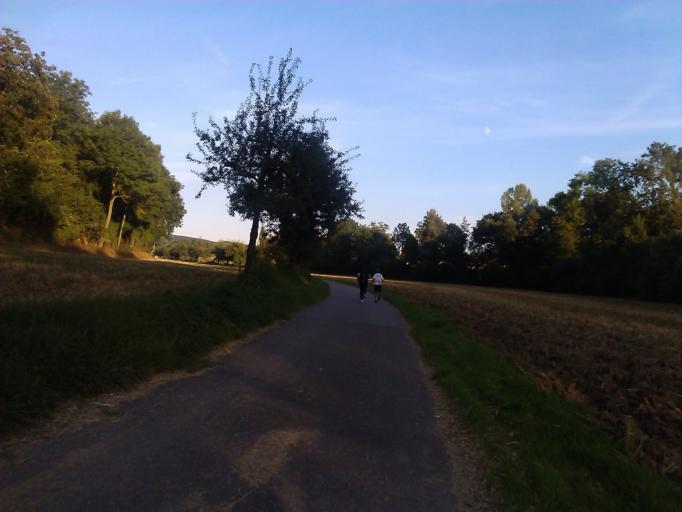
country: DE
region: Baden-Wuerttemberg
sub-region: Karlsruhe Region
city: Muhlhausen
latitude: 49.2418
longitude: 8.7573
